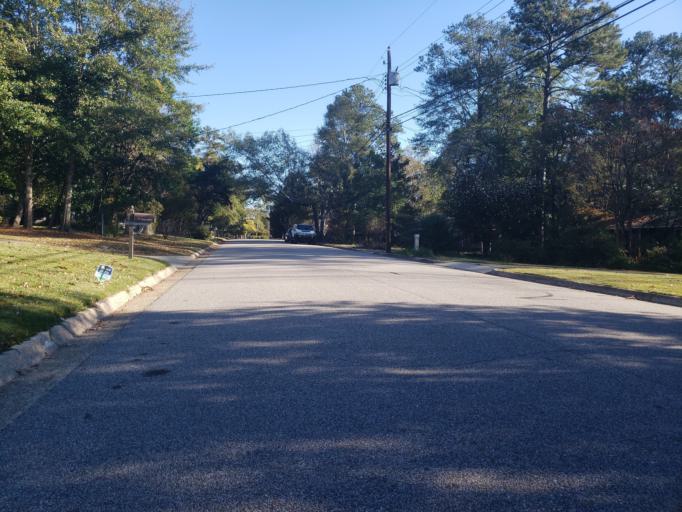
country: US
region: Alabama
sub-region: Lee County
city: Auburn
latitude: 32.5900
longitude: -85.4660
